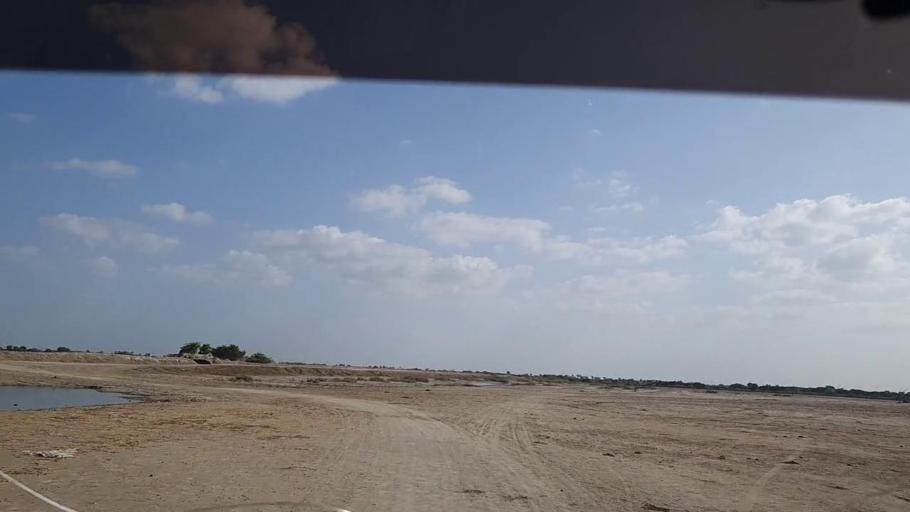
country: PK
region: Sindh
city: Kadhan
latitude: 24.4567
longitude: 68.8581
